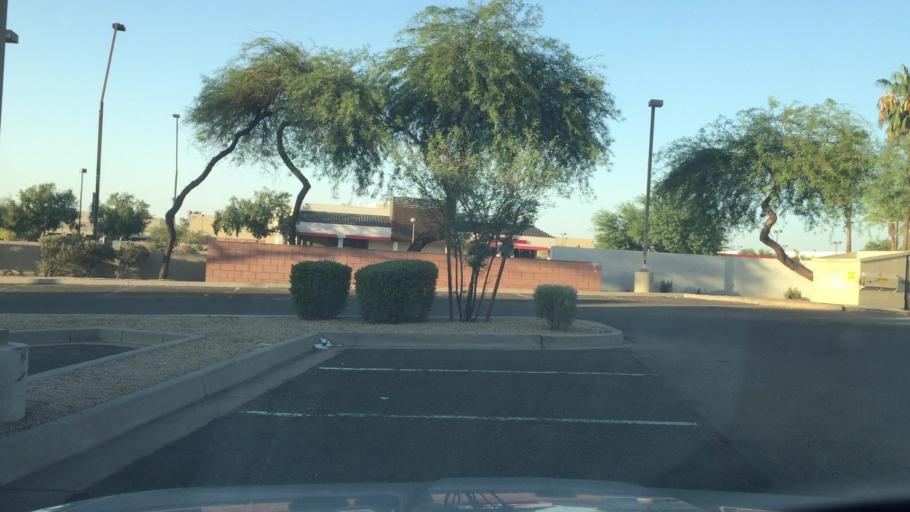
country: US
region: Arizona
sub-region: Maricopa County
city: Guadalupe
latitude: 33.3496
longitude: -111.9594
